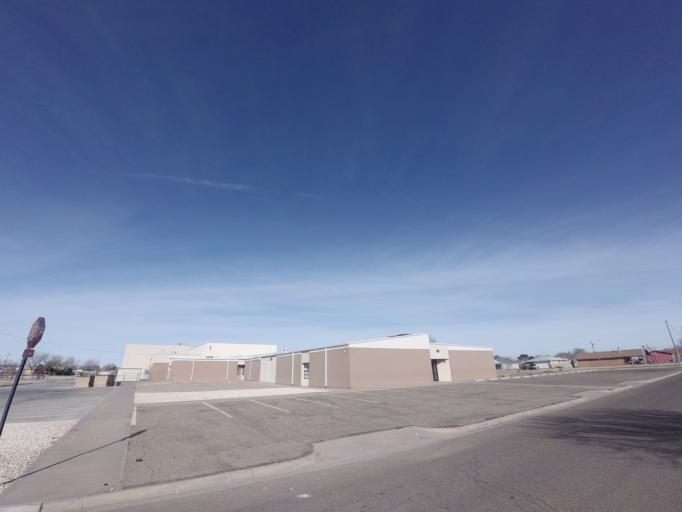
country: US
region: New Mexico
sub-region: Curry County
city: Clovis
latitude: 34.4018
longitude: -103.2179
